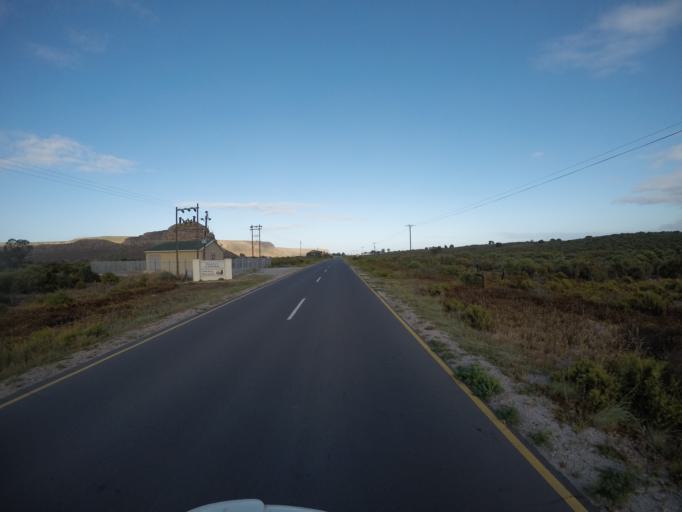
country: ZA
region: Western Cape
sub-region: West Coast District Municipality
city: Clanwilliam
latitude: -32.3128
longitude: 18.3635
